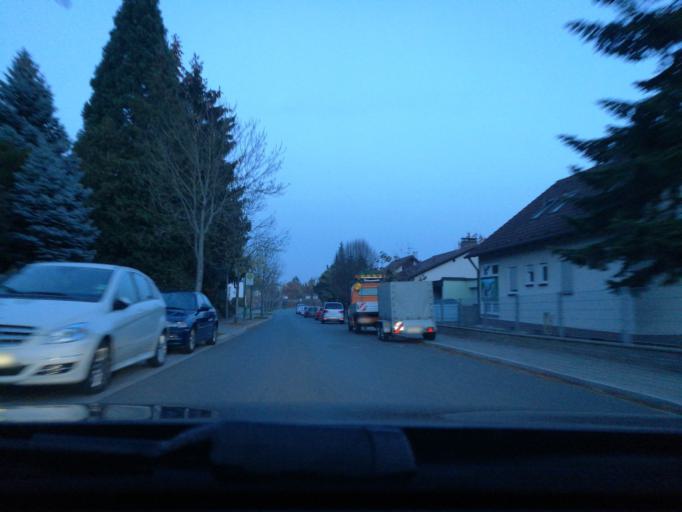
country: DE
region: Bavaria
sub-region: Regierungsbezirk Mittelfranken
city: Furth
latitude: 49.4732
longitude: 10.9601
